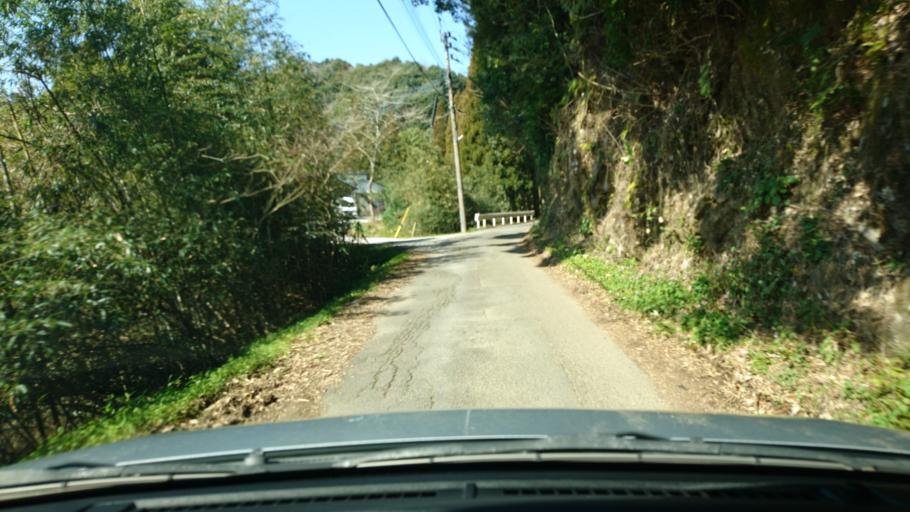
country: JP
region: Miyazaki
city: Miyazaki-shi
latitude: 31.8259
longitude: 131.3972
